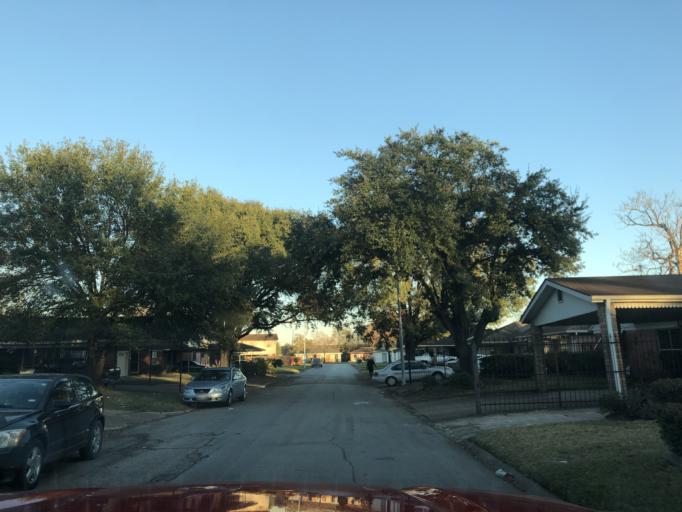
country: US
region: Texas
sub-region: Harris County
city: Jacinto City
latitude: 29.7641
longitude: -95.2679
